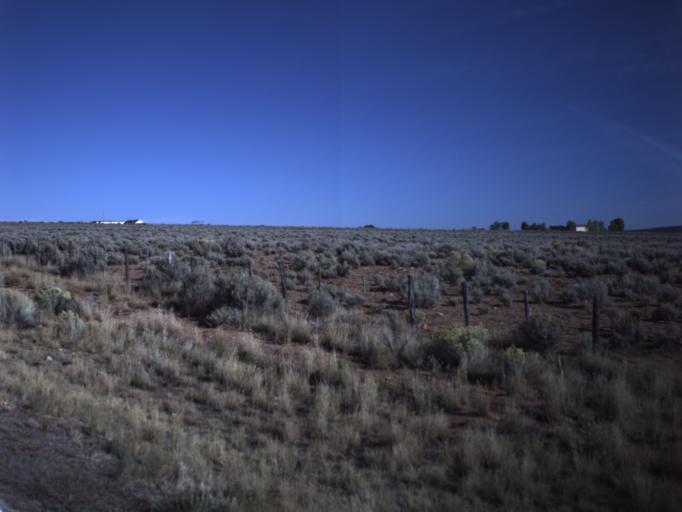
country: US
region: Utah
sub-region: Grand County
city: Moab
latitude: 38.3095
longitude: -109.2801
